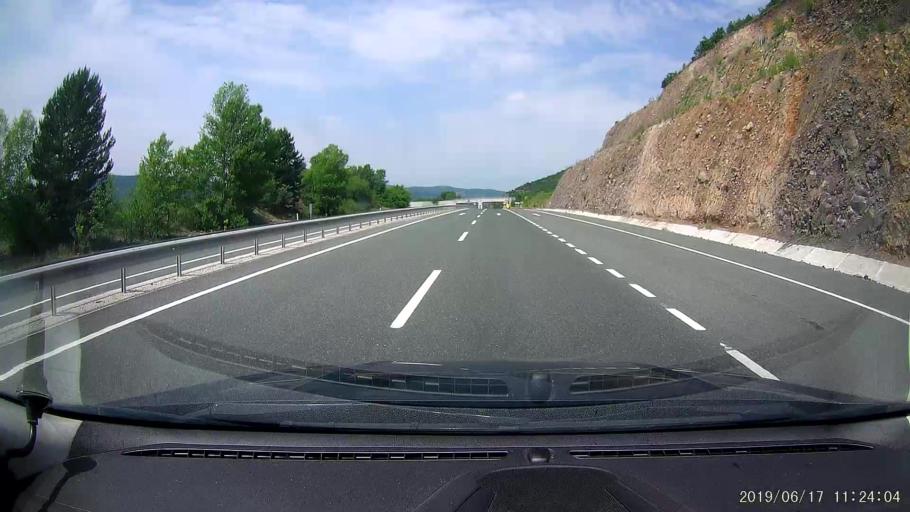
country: TR
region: Cankiri
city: Ilgaz
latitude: 40.8841
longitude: 33.7146
